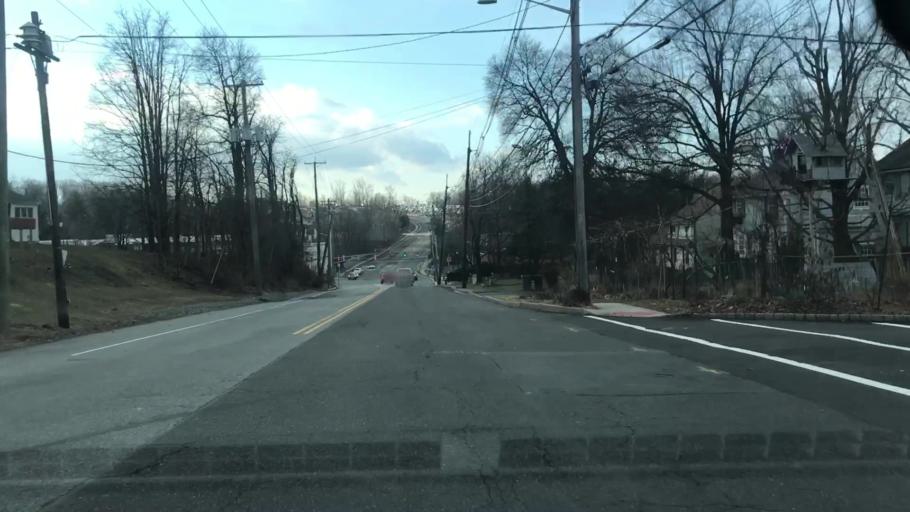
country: US
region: New Jersey
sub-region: Essex County
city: Northfield
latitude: 40.7726
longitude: -74.3009
